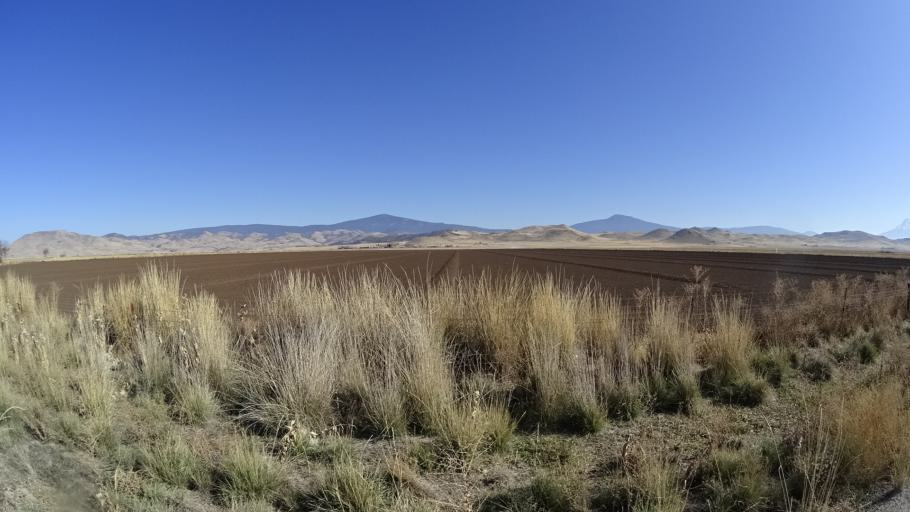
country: US
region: California
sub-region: Siskiyou County
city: Montague
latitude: 41.7878
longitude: -122.4614
